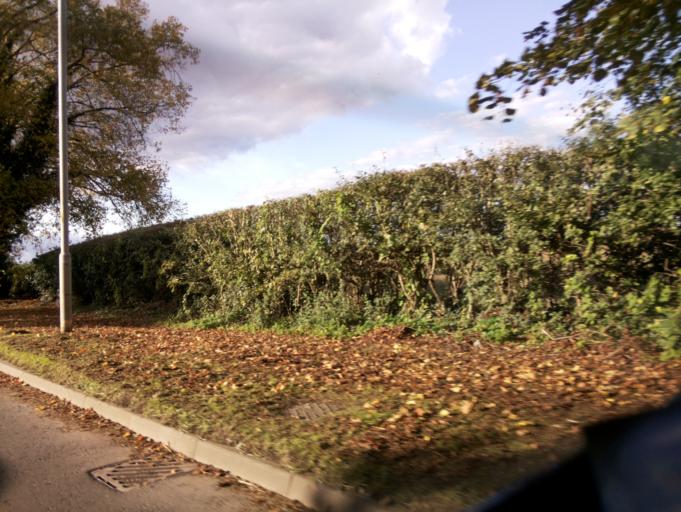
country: GB
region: England
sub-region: Herefordshire
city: Belmont
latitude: 52.0664
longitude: -2.7576
